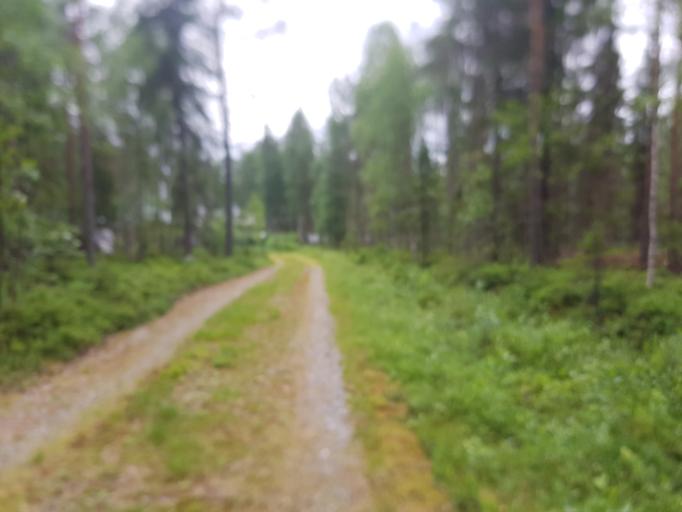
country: FI
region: Kainuu
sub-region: Kehys-Kainuu
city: Kuhmo
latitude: 64.4507
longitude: 29.7223
